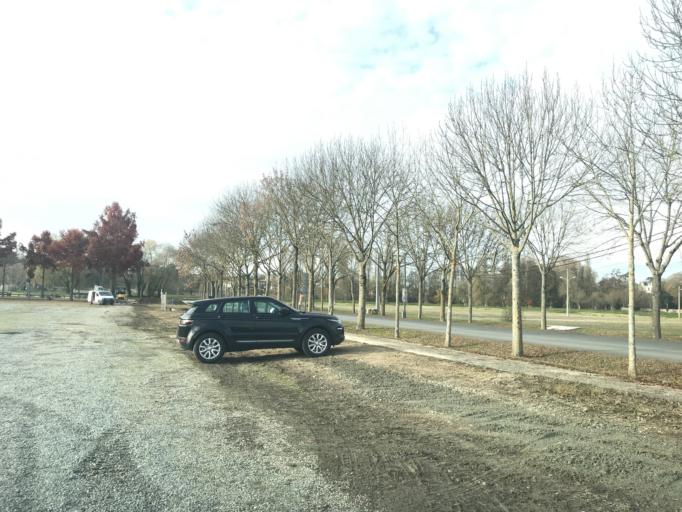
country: FR
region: Poitou-Charentes
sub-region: Departement des Deux-Sevres
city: Niort
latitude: 46.3328
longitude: -0.4887
